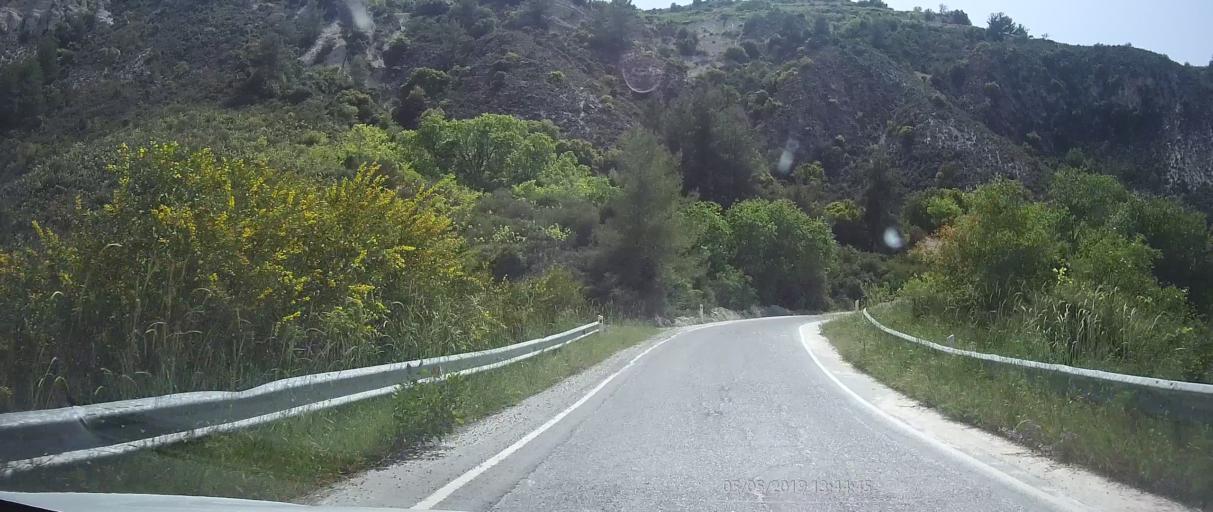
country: CY
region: Limassol
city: Pachna
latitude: 34.8680
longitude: 32.7888
